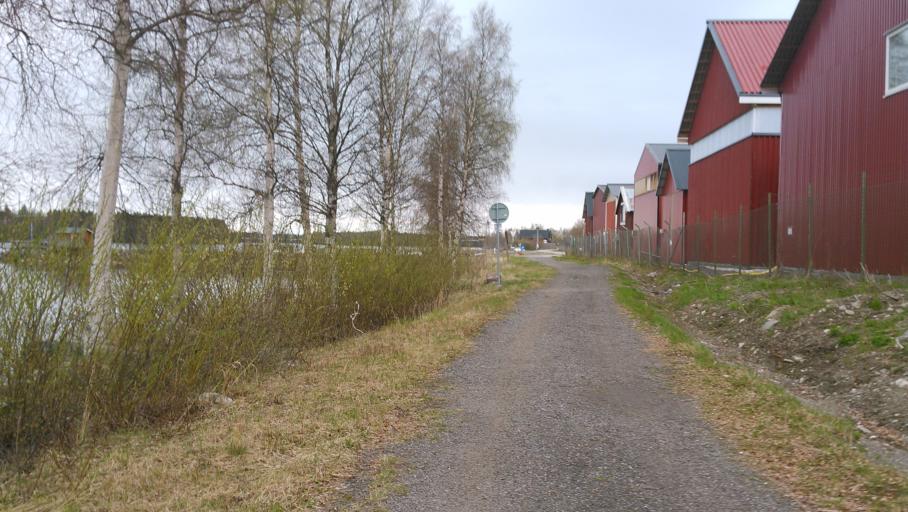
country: SE
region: Vaesterbotten
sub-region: Umea Kommun
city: Umea
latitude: 63.7876
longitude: 20.3102
